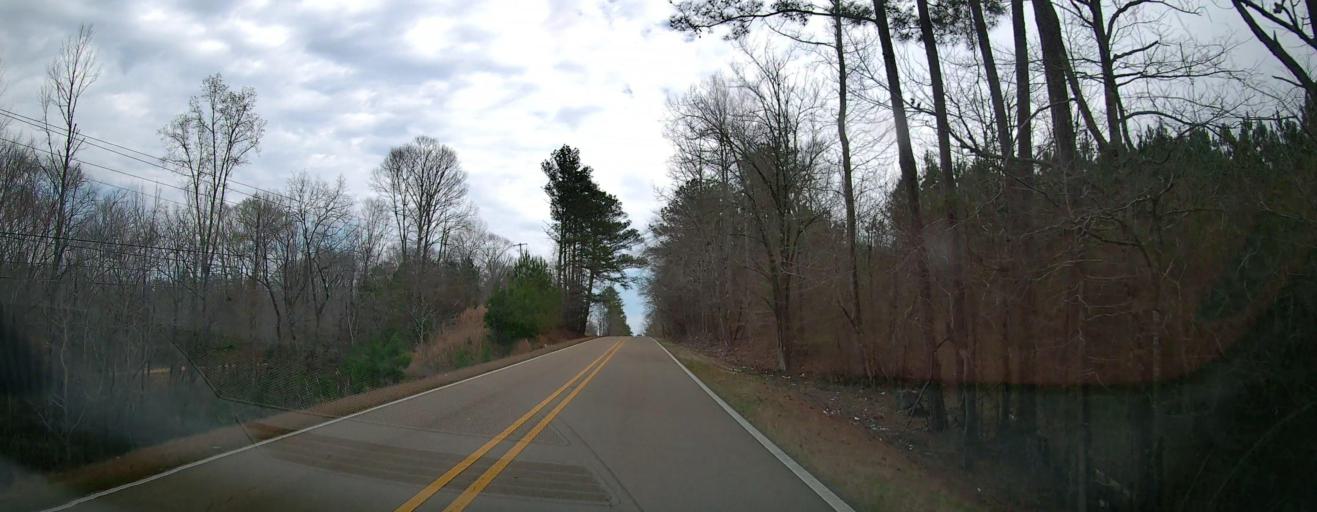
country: US
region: Mississippi
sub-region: Itawamba County
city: Fulton
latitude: 34.2483
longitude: -88.2968
